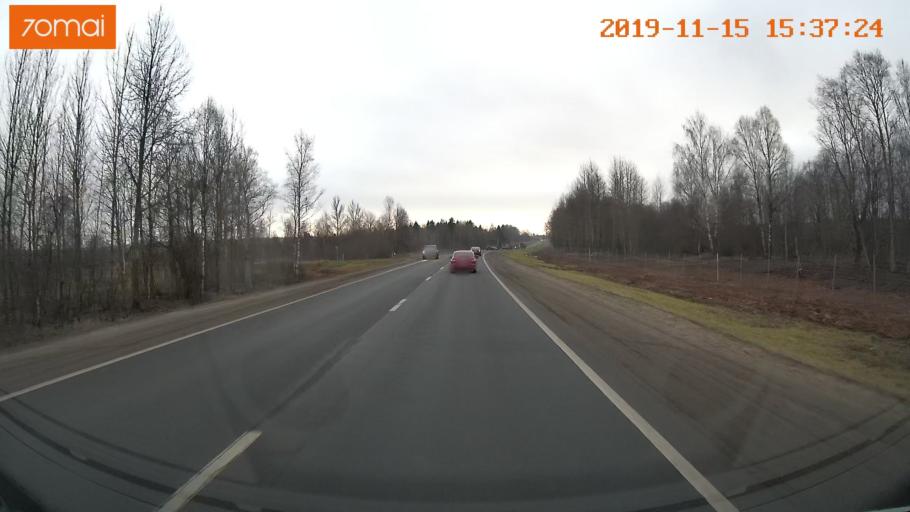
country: RU
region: Jaroslavl
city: Danilov
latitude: 58.0398
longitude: 40.0881
